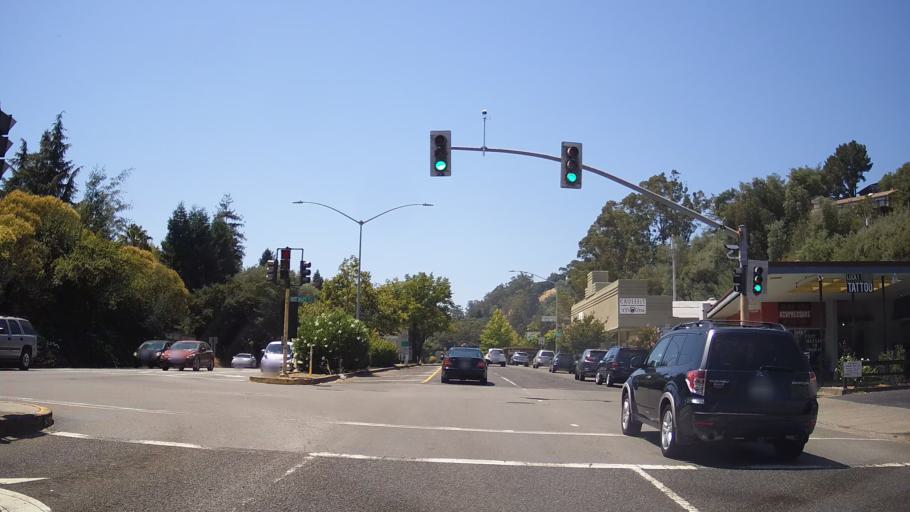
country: US
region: California
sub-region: Marin County
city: San Anselmo
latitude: 37.9763
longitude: -122.5502
